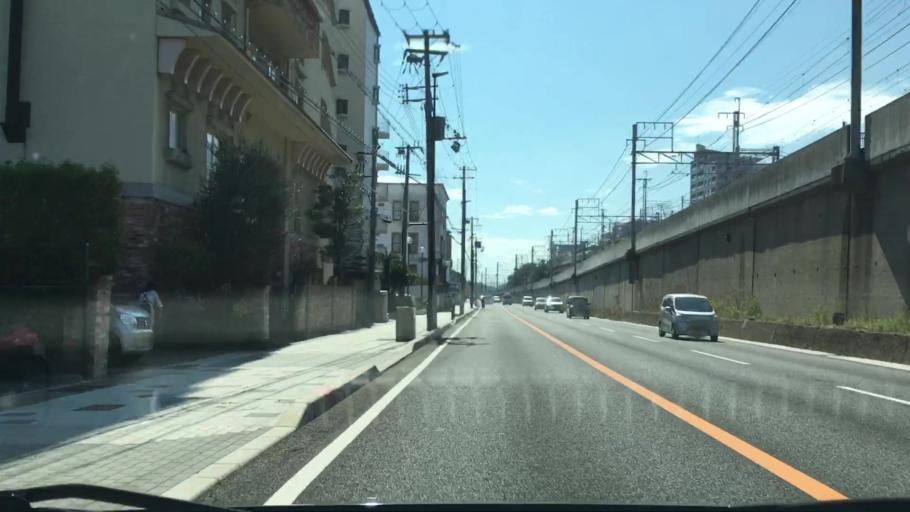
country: JP
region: Hyogo
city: Akashi
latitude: 34.6319
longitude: 135.0770
